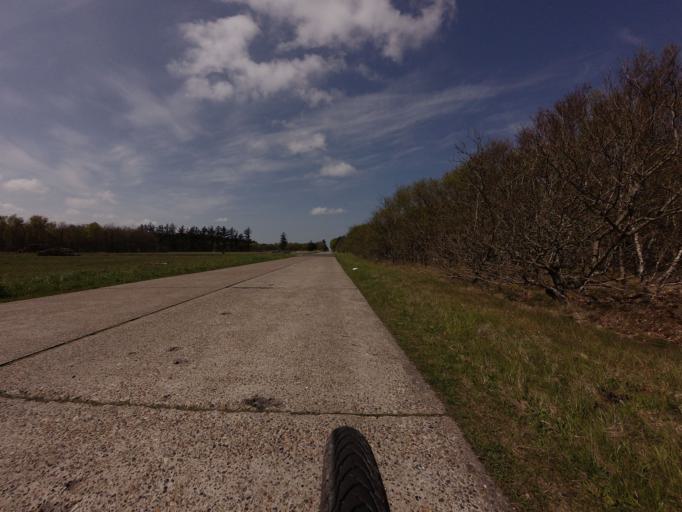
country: DK
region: North Denmark
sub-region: Jammerbugt Kommune
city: Brovst
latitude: 57.1661
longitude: 9.4779
